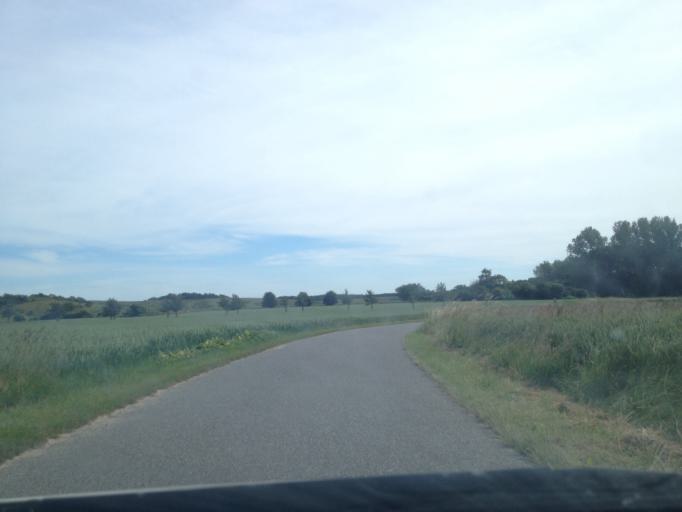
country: DK
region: Central Jutland
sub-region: Samso Kommune
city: Tranebjerg
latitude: 55.7850
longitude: 10.5537
